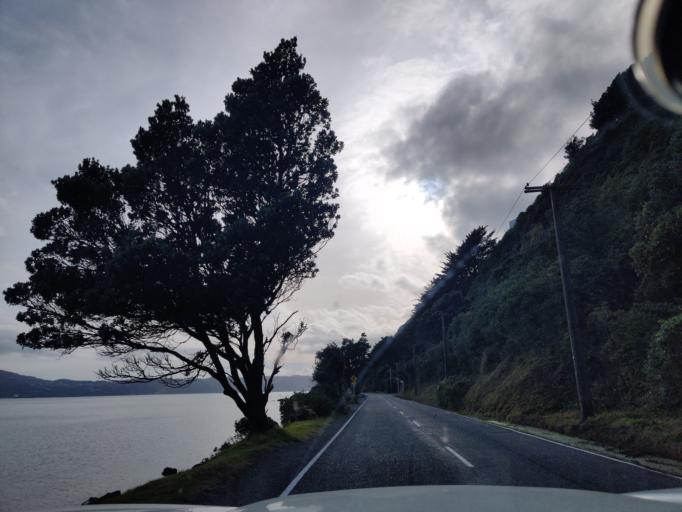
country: NZ
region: Wellington
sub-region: Wellington City
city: Wellington
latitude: -41.3096
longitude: 174.8131
